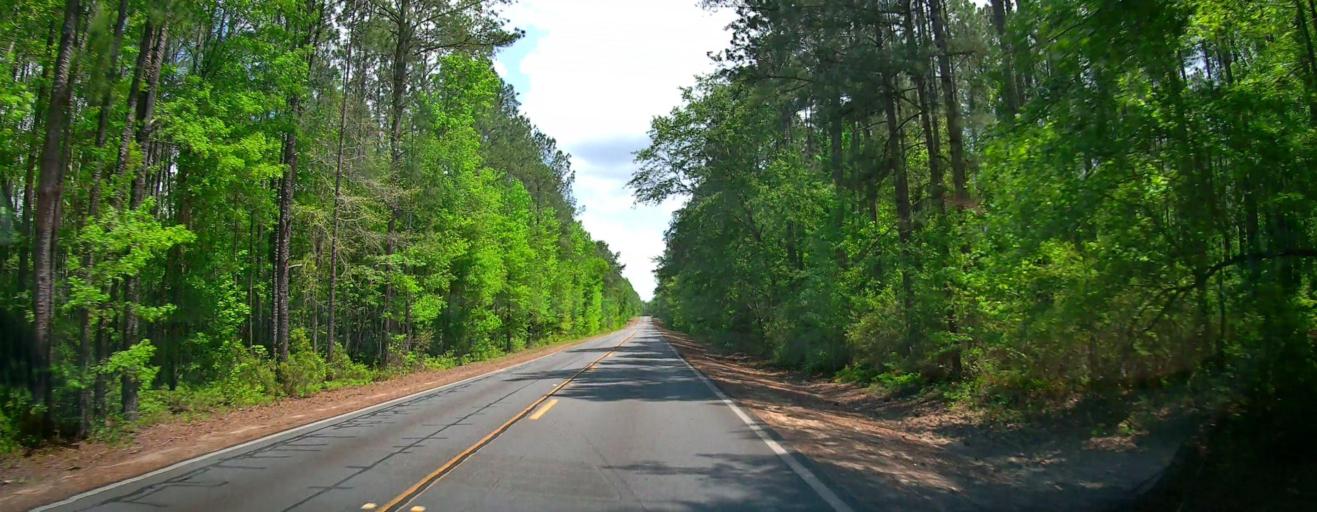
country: US
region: Georgia
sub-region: Treutlen County
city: Soperton
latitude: 32.5057
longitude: -82.6221
